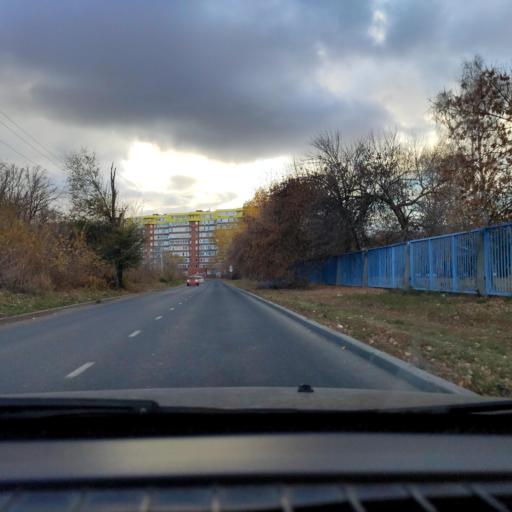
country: RU
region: Samara
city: Tol'yatti
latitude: 53.5195
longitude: 49.3196
